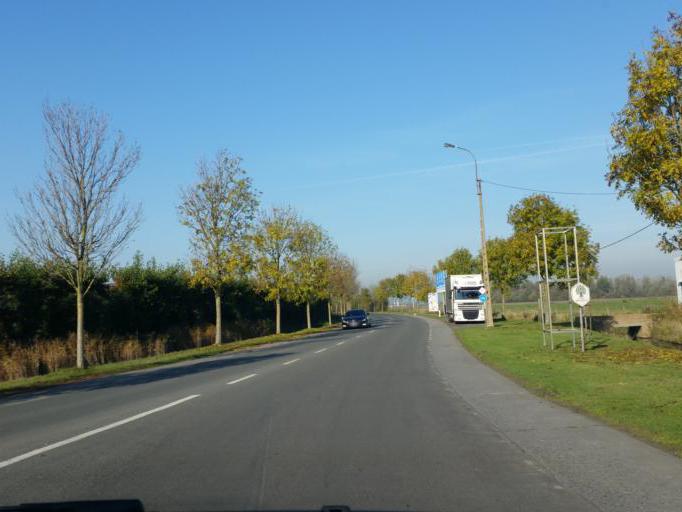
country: BE
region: Flanders
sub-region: Provincie West-Vlaanderen
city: De Haan
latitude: 51.2307
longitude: 3.0401
